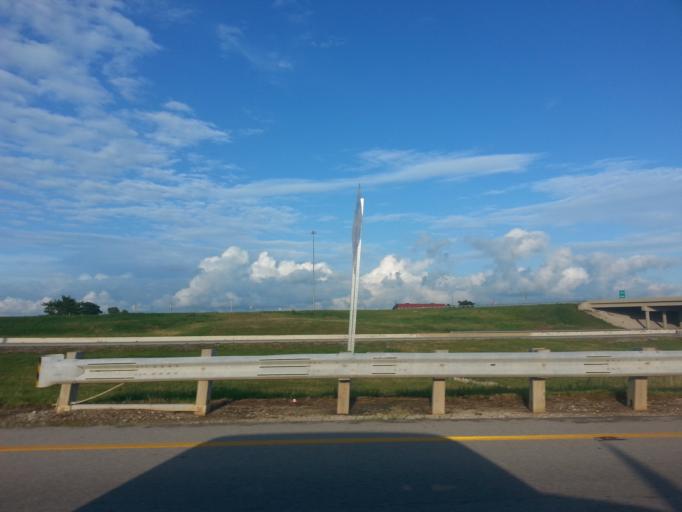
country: US
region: Kentucky
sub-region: Madison County
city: Richmond
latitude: 37.6757
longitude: -84.3130
